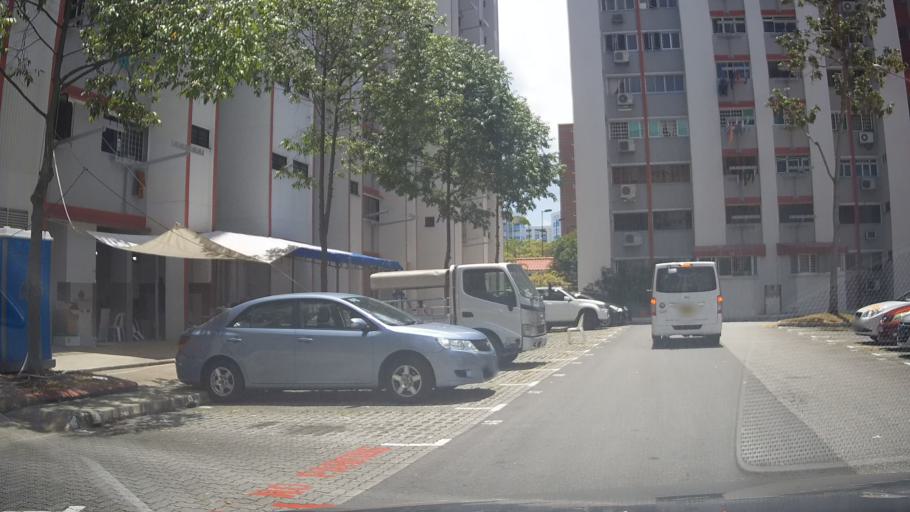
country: SG
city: Singapore
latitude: 1.3577
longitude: 103.9517
